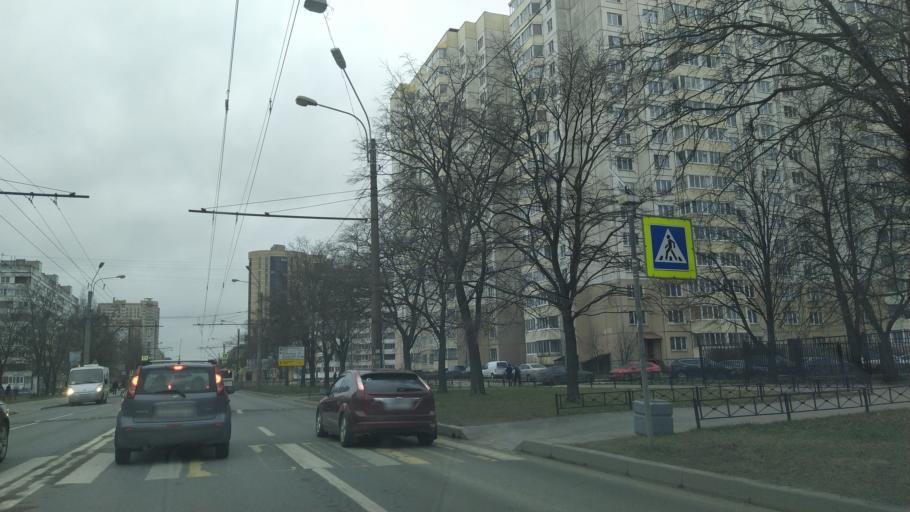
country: RU
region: St.-Petersburg
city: Komendantsky aerodrom
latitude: 60.0105
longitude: 30.2870
